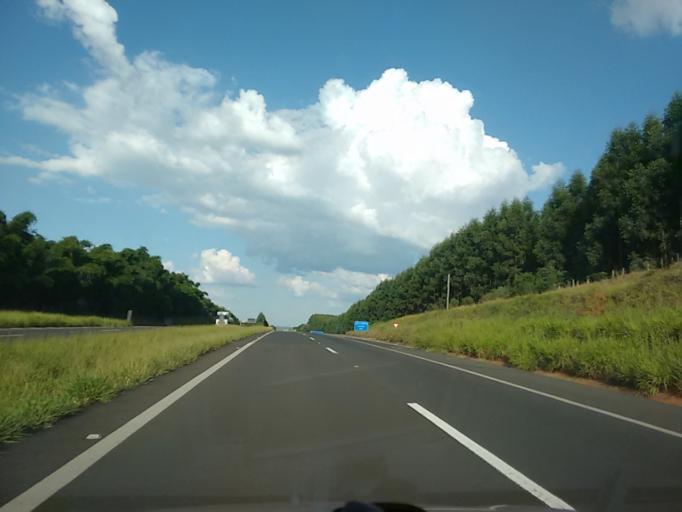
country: BR
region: Sao Paulo
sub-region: Duartina
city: Duartina
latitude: -22.3296
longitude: -49.4500
